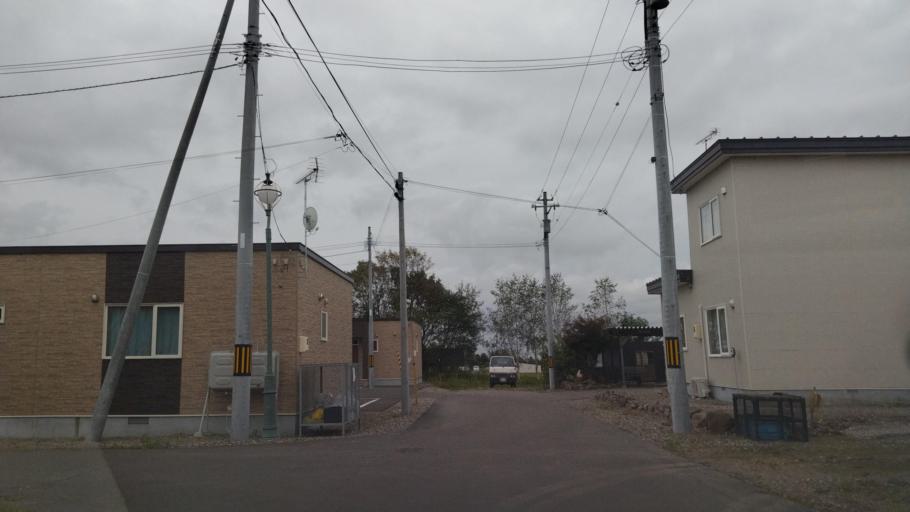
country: JP
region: Hokkaido
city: Otofuke
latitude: 43.2296
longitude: 143.2863
